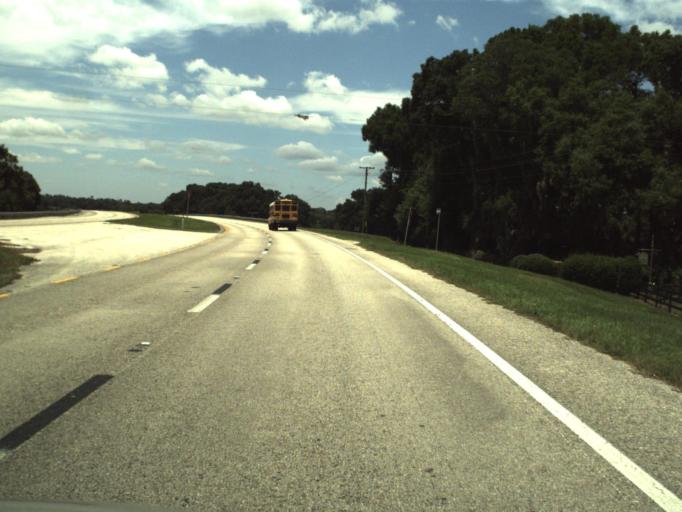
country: US
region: Florida
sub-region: Marion County
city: Citra
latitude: 29.3973
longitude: -82.1984
